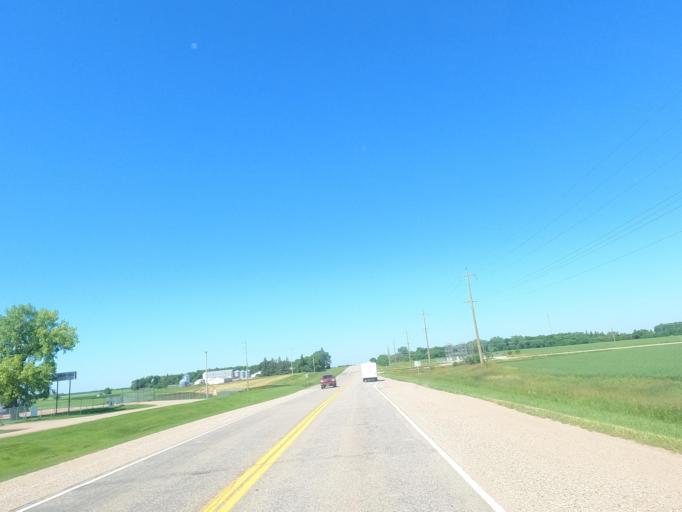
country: CA
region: Manitoba
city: Brandon
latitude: 49.5771
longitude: -99.6728
